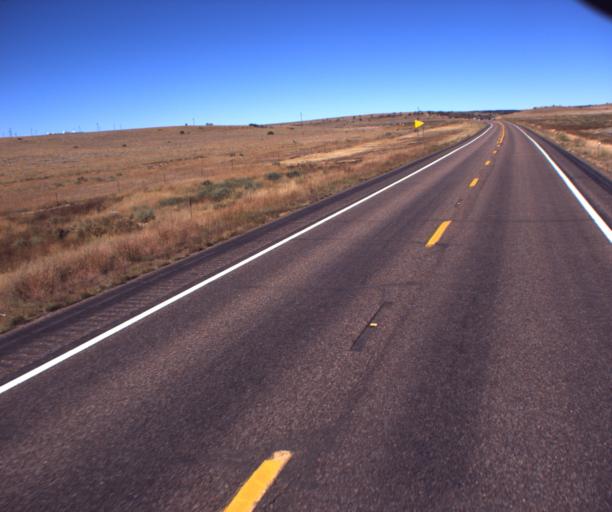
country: US
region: Arizona
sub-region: Apache County
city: Saint Johns
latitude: 34.3186
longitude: -109.3823
